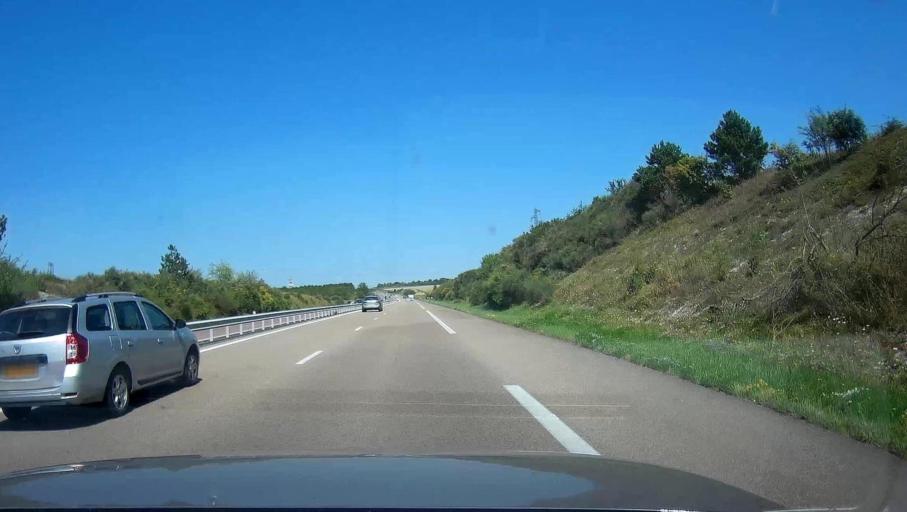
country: FR
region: Champagne-Ardenne
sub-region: Departement de l'Aube
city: Creney-pres-Troyes
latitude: 48.3514
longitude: 4.1652
